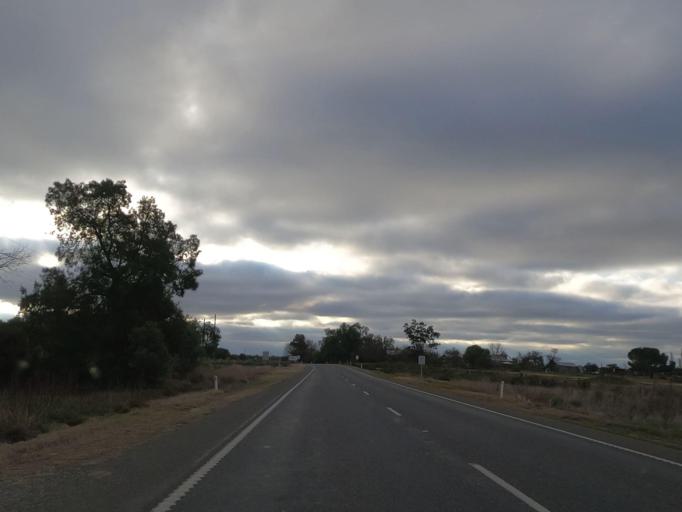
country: AU
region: Victoria
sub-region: Swan Hill
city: Swan Hill
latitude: -35.7256
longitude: 143.8905
